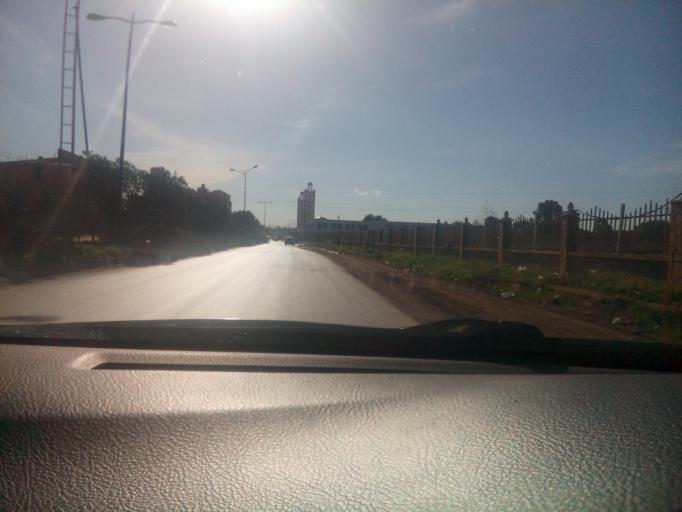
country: DZ
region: Oran
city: Sidi ech Chahmi
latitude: 35.6558
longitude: -0.5679
